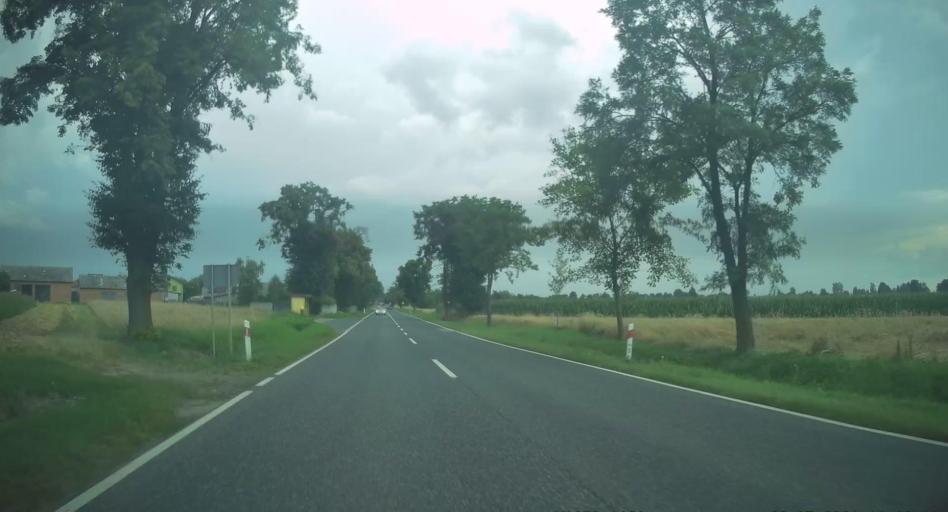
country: PL
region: Lodz Voivodeship
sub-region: Powiat skierniewicki
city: Gluchow
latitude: 51.7827
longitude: 20.0587
